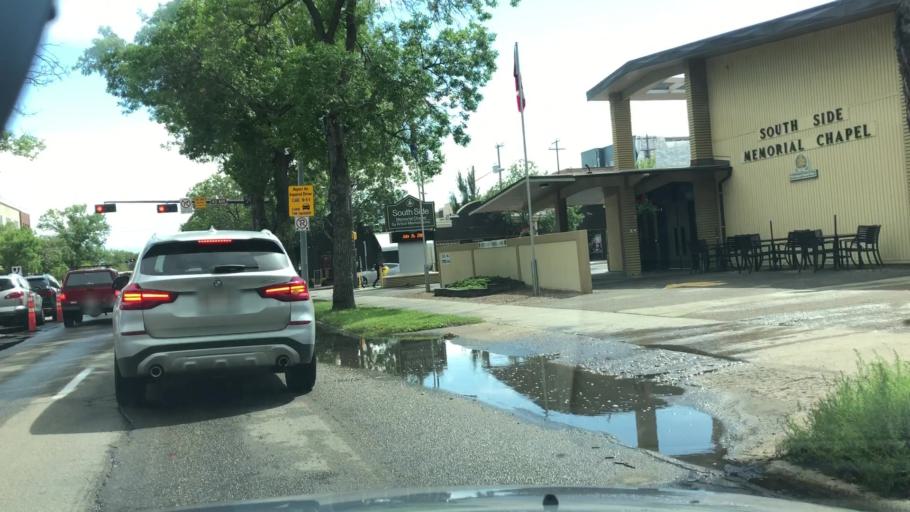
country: CA
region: Alberta
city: Edmonton
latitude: 53.5196
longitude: -113.4977
